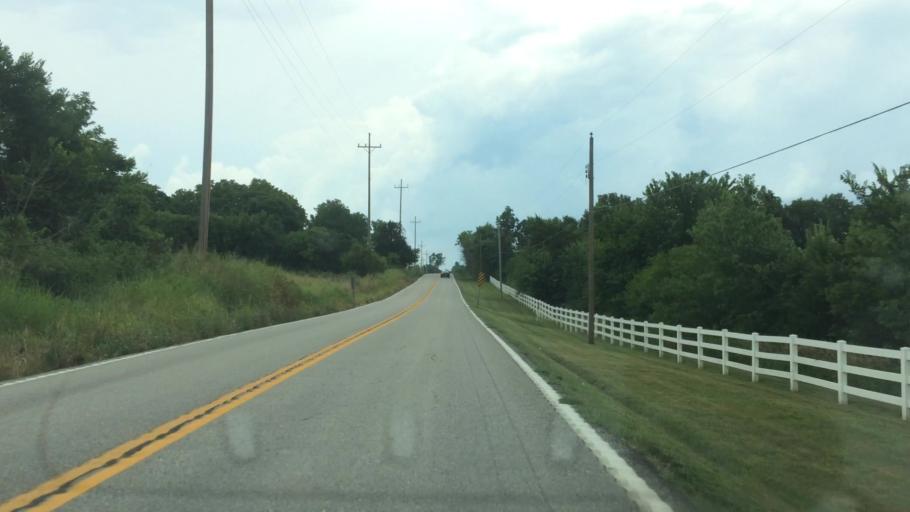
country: US
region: Missouri
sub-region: Greene County
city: Strafford
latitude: 37.2570
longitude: -93.1352
